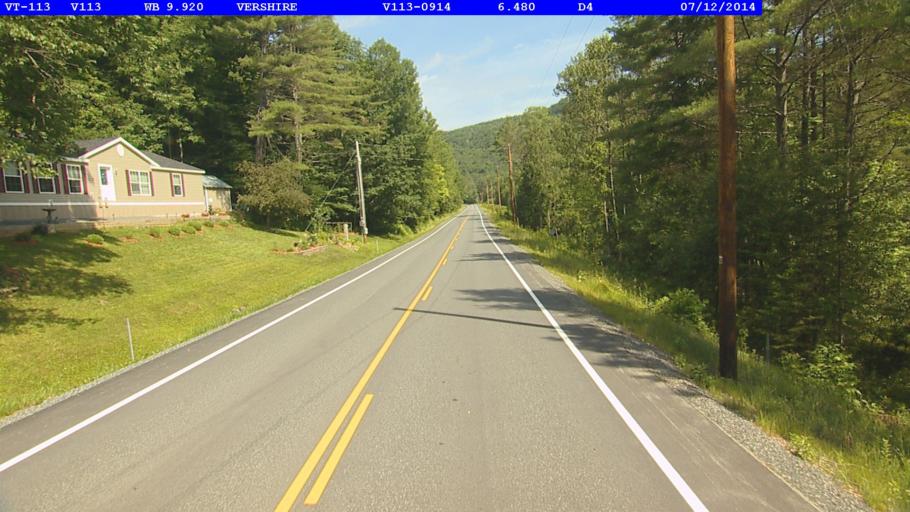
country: US
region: New Hampshire
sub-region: Grafton County
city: Orford
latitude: 43.9519
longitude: -72.2769
